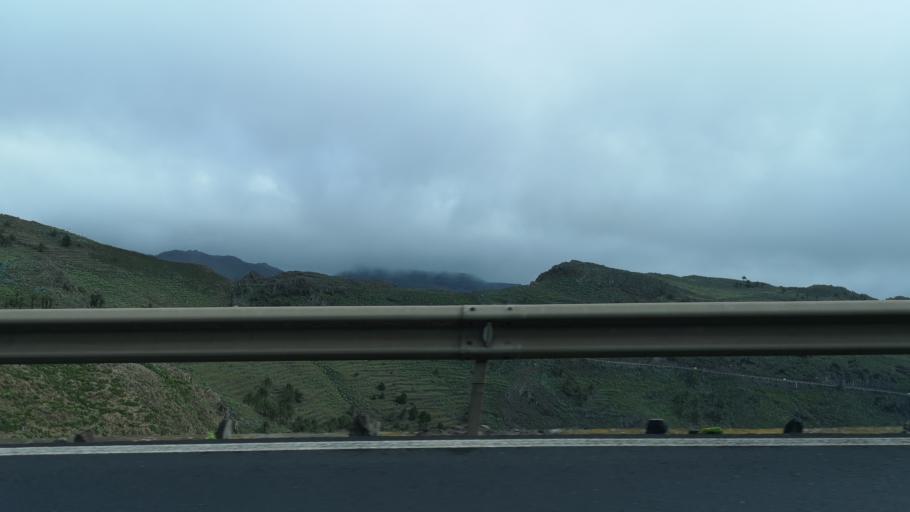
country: ES
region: Canary Islands
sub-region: Provincia de Santa Cruz de Tenerife
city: San Sebastian de la Gomera
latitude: 28.0971
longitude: -17.1721
